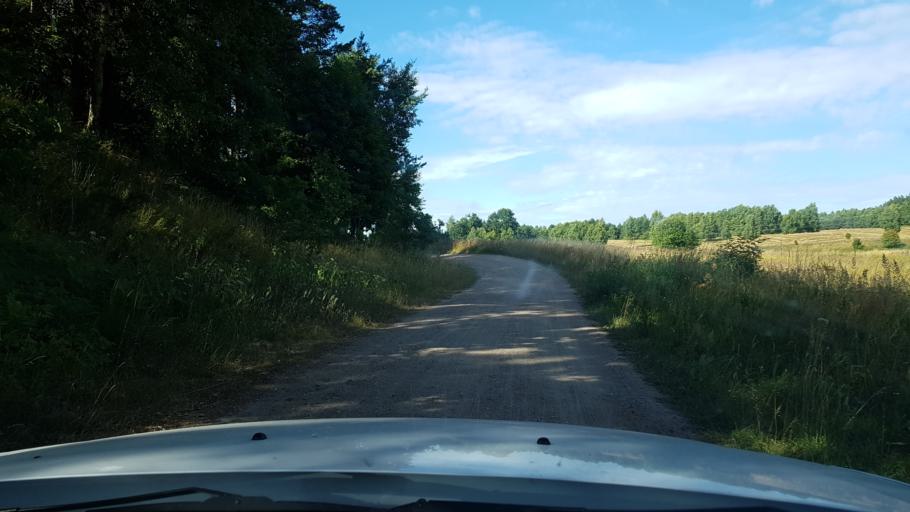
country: PL
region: West Pomeranian Voivodeship
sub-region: Powiat drawski
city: Zlocieniec
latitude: 53.6396
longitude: 16.0401
